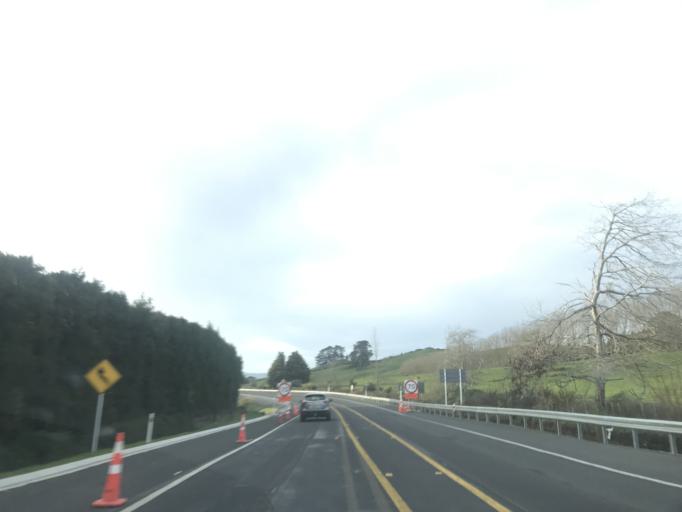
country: NZ
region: Bay of Plenty
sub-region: Western Bay of Plenty District
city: Waihi Beach
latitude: -37.4470
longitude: 175.8783
